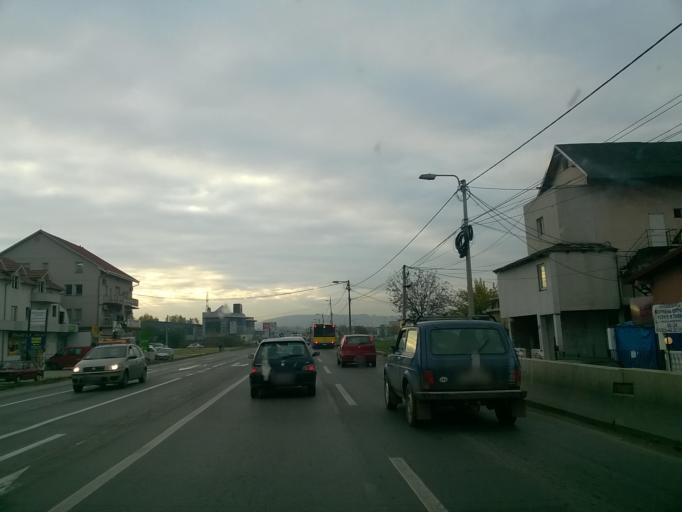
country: RS
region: Central Serbia
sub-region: Belgrade
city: Stari Grad
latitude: 44.8444
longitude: 20.4892
